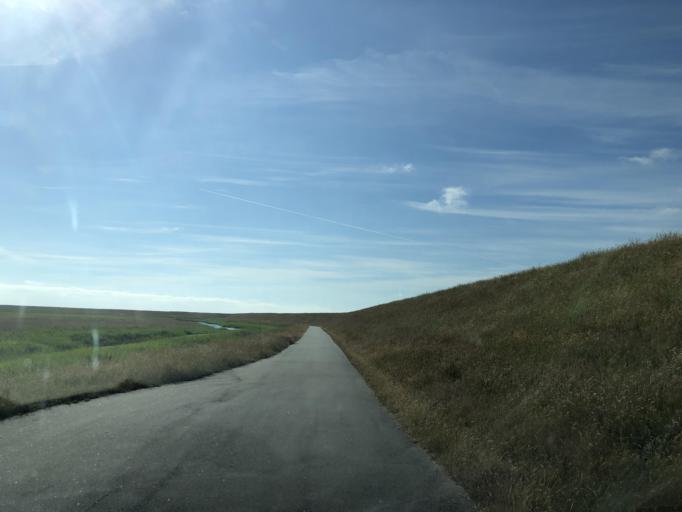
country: DK
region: South Denmark
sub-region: Esbjerg Kommune
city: Tjaereborg
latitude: 55.2932
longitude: 8.5647
